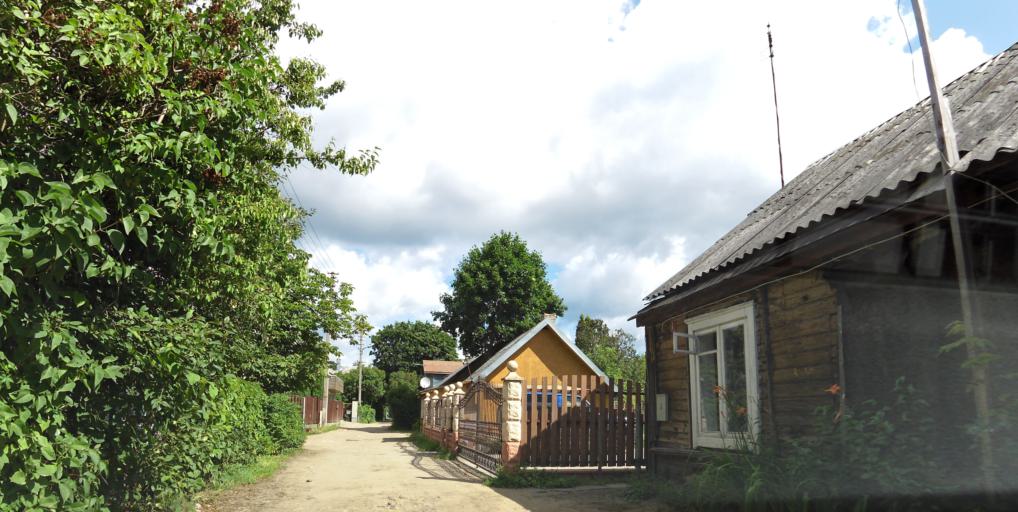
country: LT
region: Vilnius County
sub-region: Vilnius
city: Vilnius
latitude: 54.6988
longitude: 25.2799
